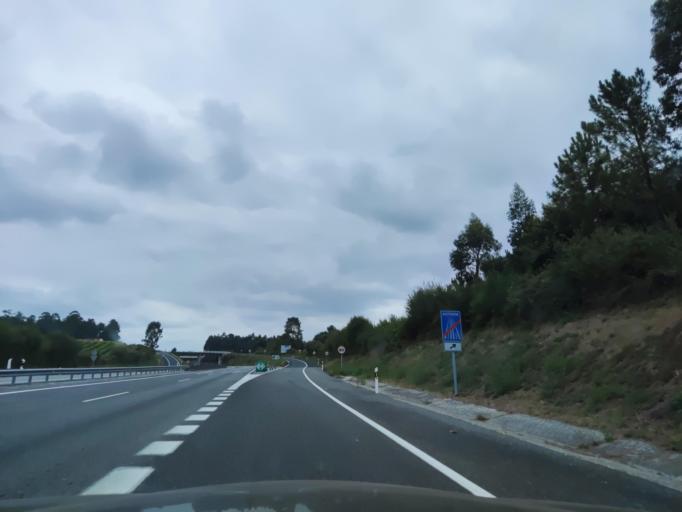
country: ES
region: Galicia
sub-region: Provincia da Coruna
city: Teo
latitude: 42.7964
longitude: -8.5386
